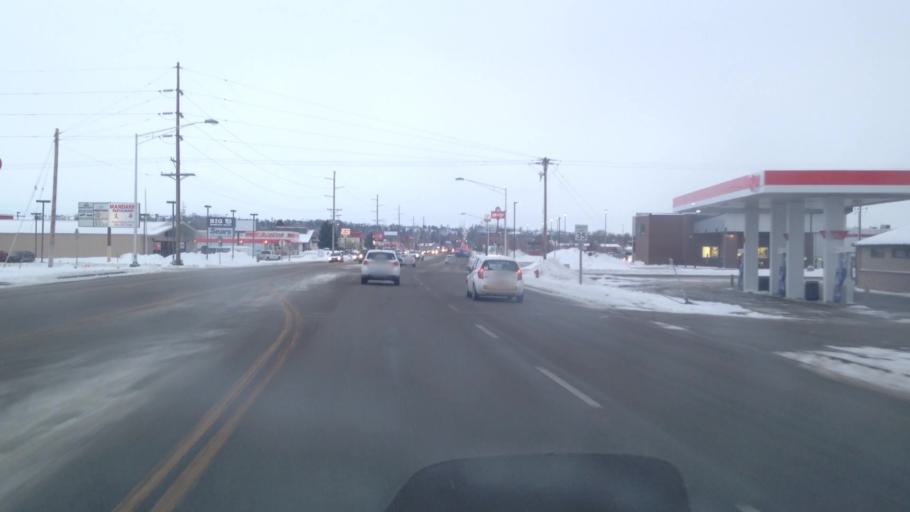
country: US
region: Idaho
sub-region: Madison County
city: Rexburg
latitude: 43.8411
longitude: -111.7782
